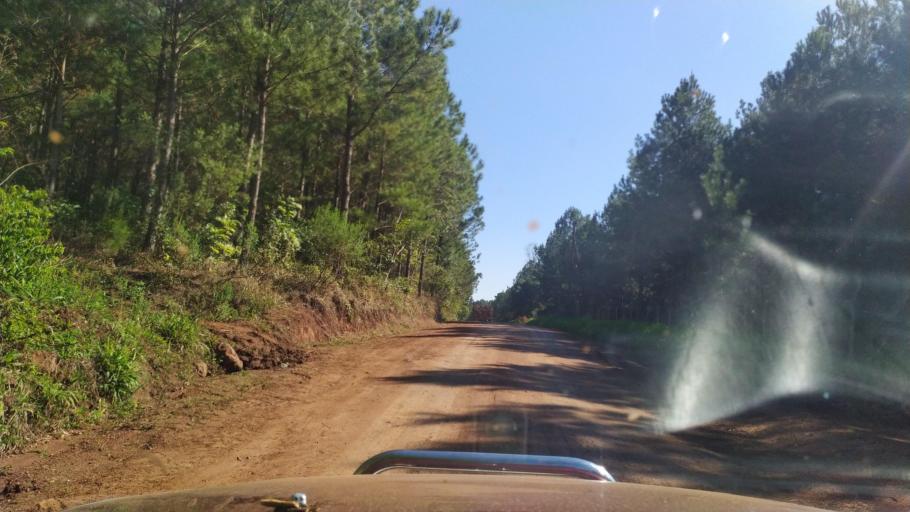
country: AR
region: Misiones
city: El Alcazar
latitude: -26.7374
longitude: -54.6448
